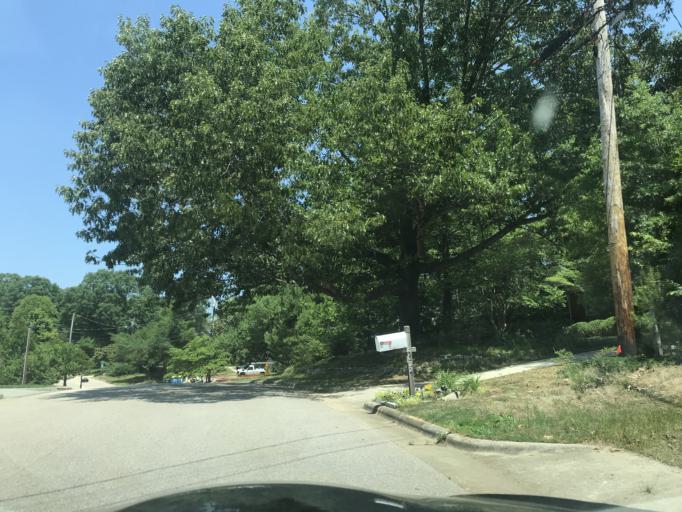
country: US
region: North Carolina
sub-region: Wake County
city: West Raleigh
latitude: 35.8498
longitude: -78.6453
